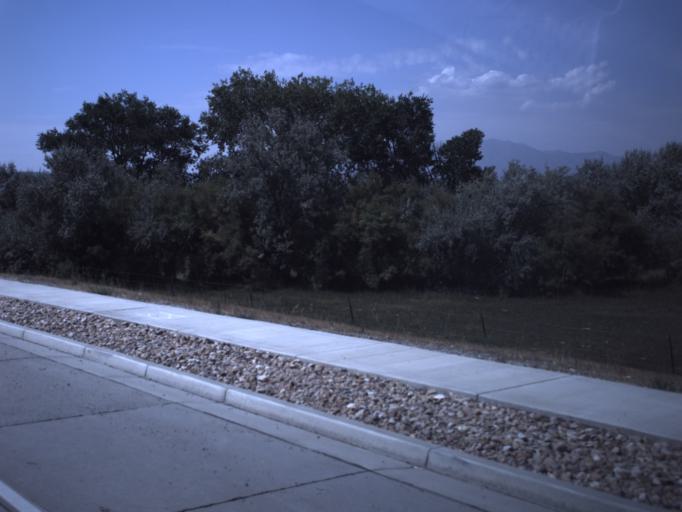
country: US
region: Utah
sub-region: Utah County
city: Saratoga Springs
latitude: 40.3754
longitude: -111.9032
